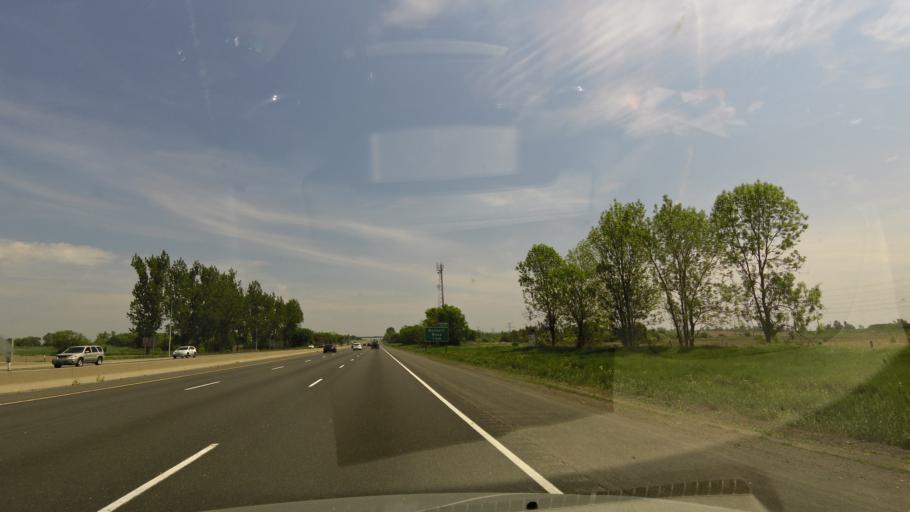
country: CA
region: Ontario
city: Oshawa
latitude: 43.9005
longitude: -78.6576
